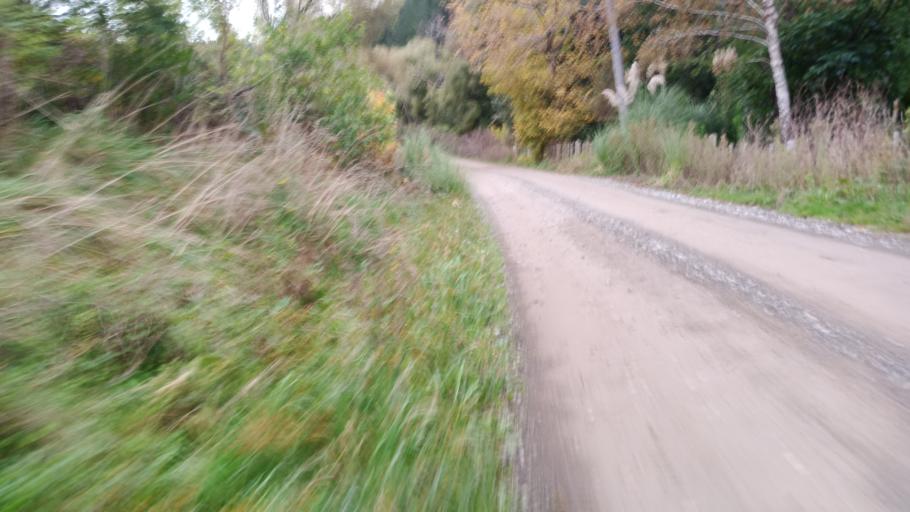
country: NZ
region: Gisborne
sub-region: Gisborne District
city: Gisborne
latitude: -38.6493
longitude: 178.0420
